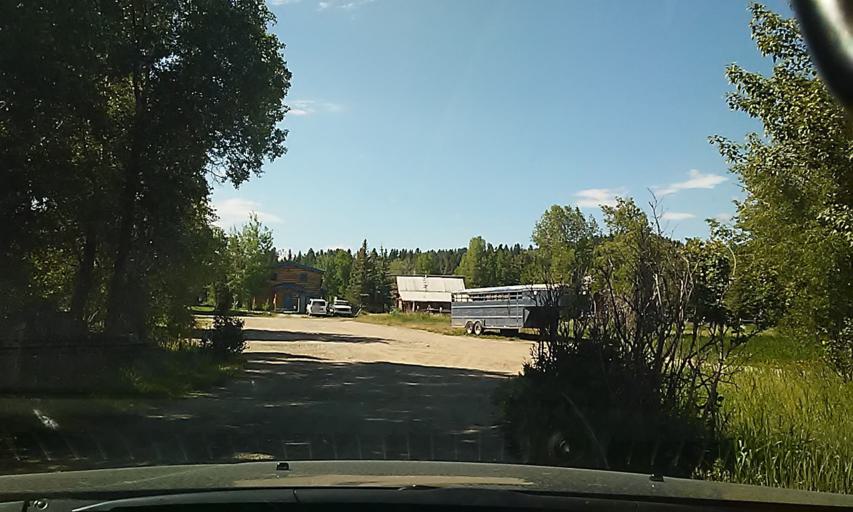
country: US
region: Wyoming
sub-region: Teton County
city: Jackson
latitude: 43.6223
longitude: -110.6278
